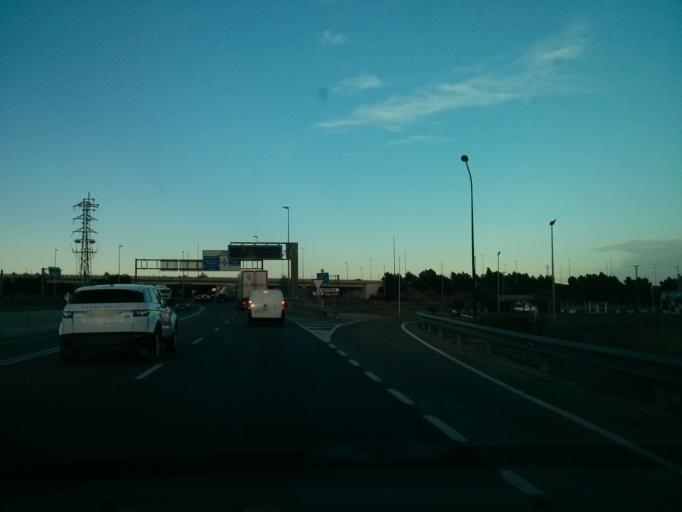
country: ES
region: Catalonia
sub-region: Provincia de Tarragona
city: El Vendrell
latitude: 41.1928
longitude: 1.5241
